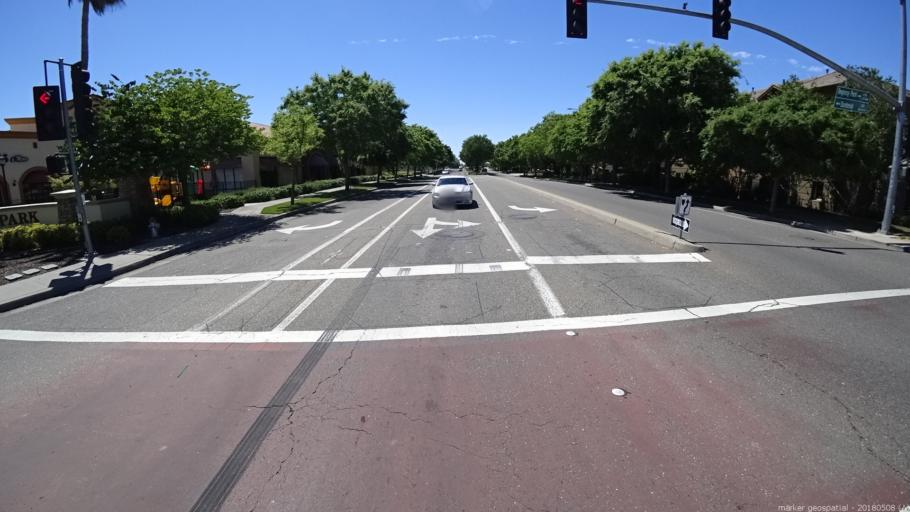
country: US
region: California
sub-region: Sacramento County
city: Rio Linda
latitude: 38.6708
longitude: -121.5045
